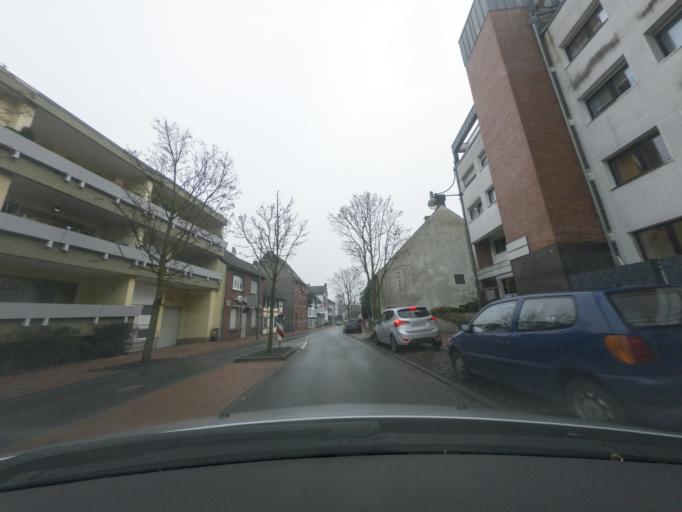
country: DE
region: North Rhine-Westphalia
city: Waltrop
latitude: 51.6232
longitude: 7.3919
